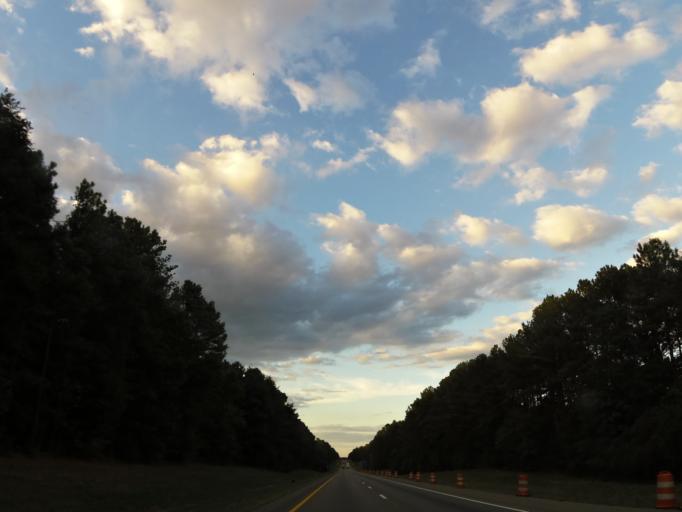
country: US
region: Tennessee
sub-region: Bradley County
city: Hopewell
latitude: 35.2566
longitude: -84.8349
